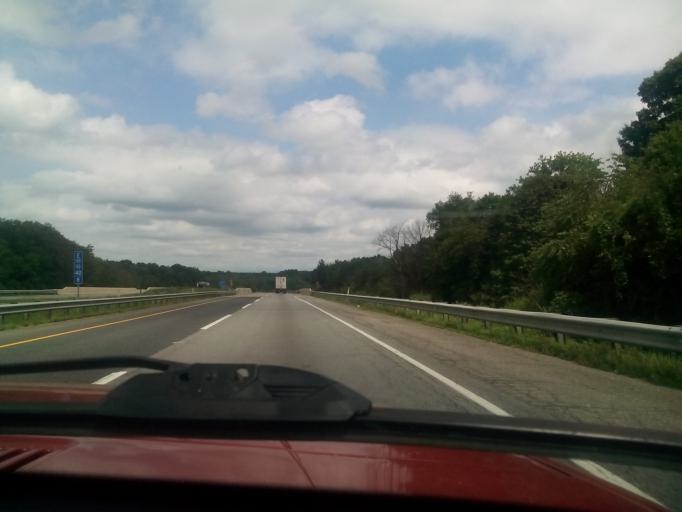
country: US
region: Indiana
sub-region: LaPorte County
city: Westville
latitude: 41.5988
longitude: -86.8656
